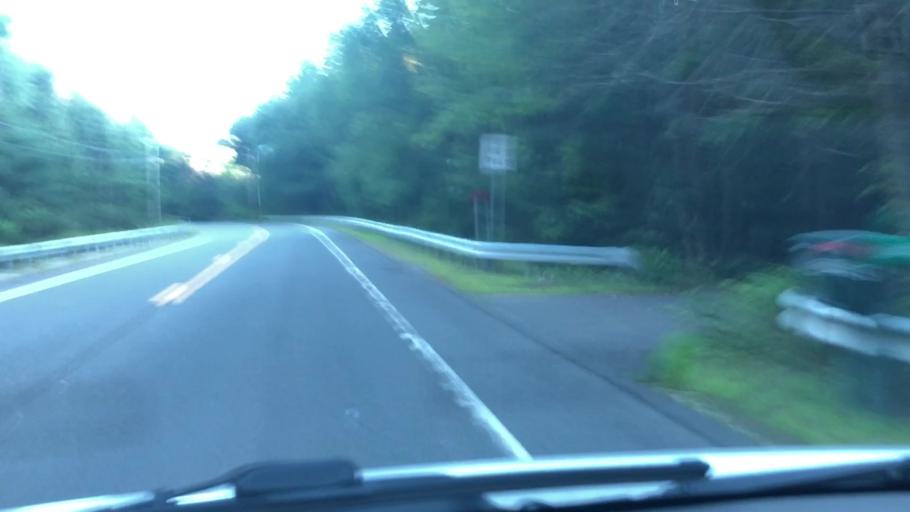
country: US
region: Massachusetts
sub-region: Hampshire County
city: Westhampton
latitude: 42.2847
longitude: -72.7961
